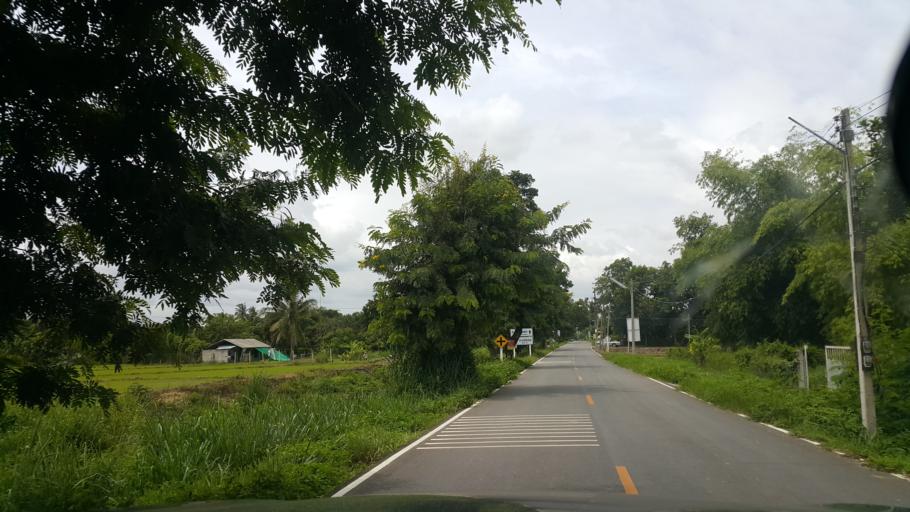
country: TH
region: Chiang Mai
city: San Kamphaeng
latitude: 18.7521
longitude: 99.1669
